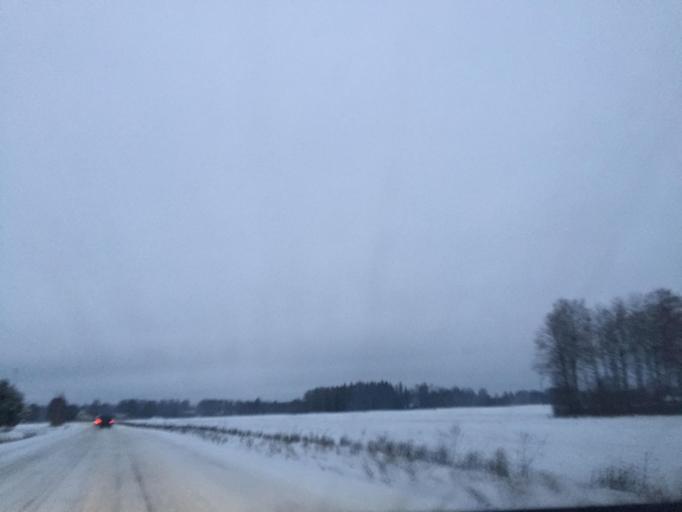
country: LV
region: Raunas
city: Rauna
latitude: 57.4274
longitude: 25.5972
